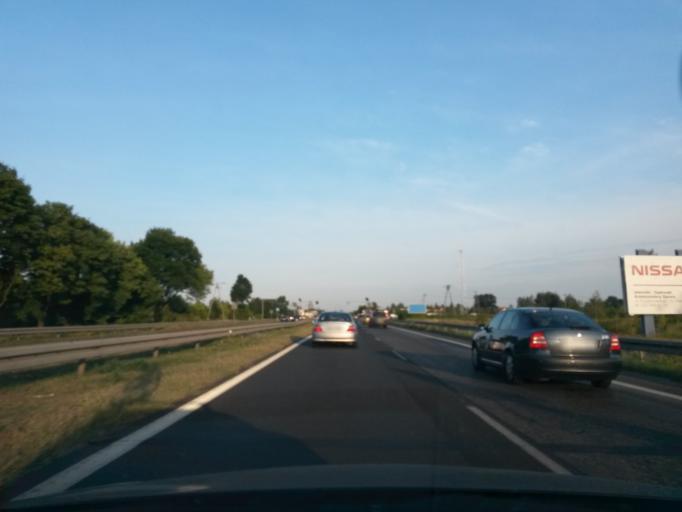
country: PL
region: Masovian Voivodeship
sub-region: Powiat warszawski zachodni
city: Dziekanow Lesny
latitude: 52.3558
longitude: 20.8407
